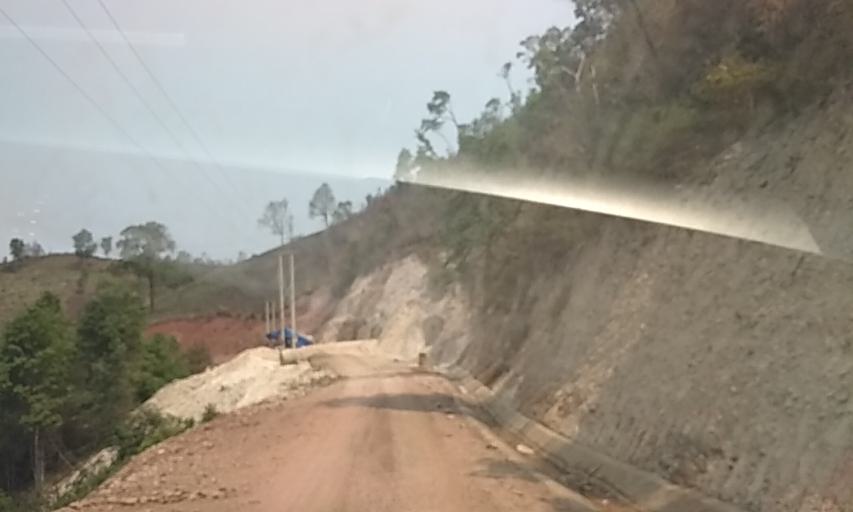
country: VN
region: Huyen Dien Bien
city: Dien Bien Phu
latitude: 21.4813
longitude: 102.7801
